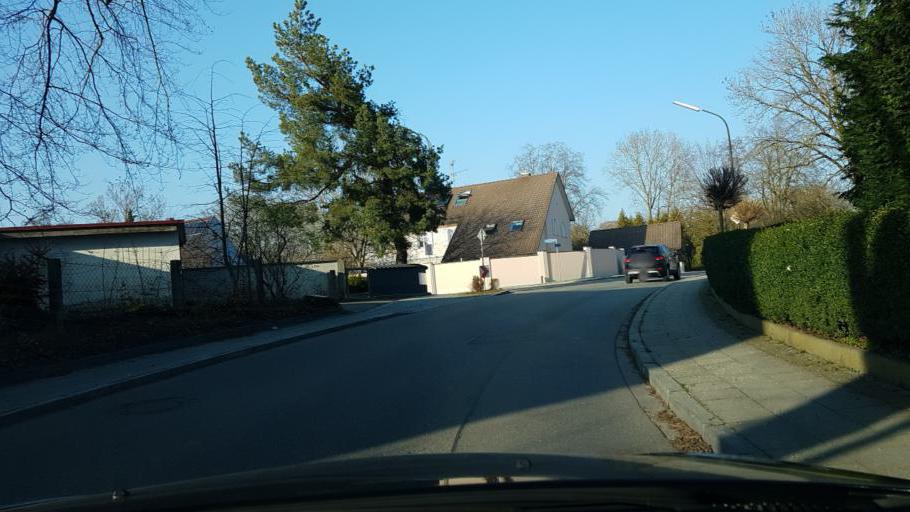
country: DE
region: Bavaria
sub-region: Upper Bavaria
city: Odelzhausen
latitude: 48.3117
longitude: 11.1989
